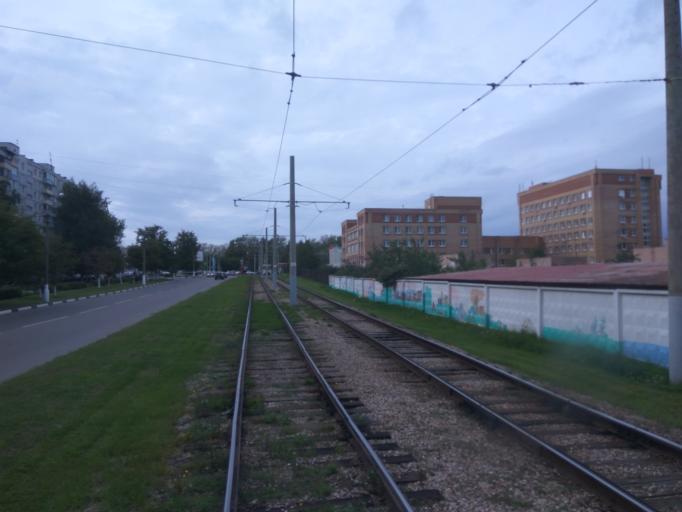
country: RU
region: Moskovskaya
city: Kolomna
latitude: 55.0656
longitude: 38.7561
